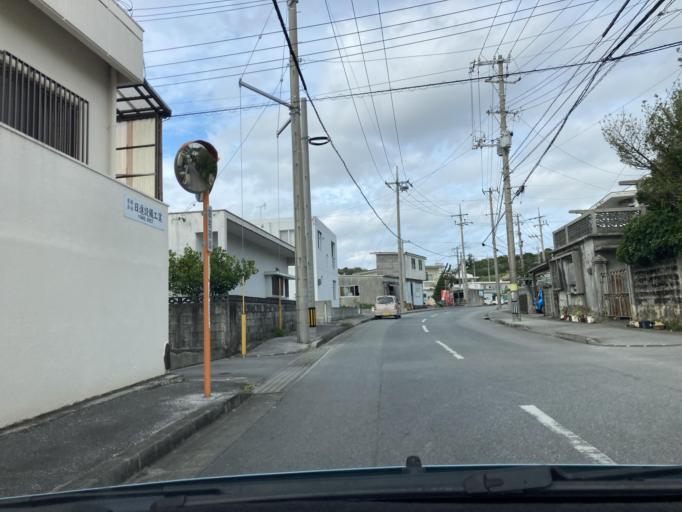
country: JP
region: Okinawa
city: Ginowan
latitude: 26.2060
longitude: 127.7475
